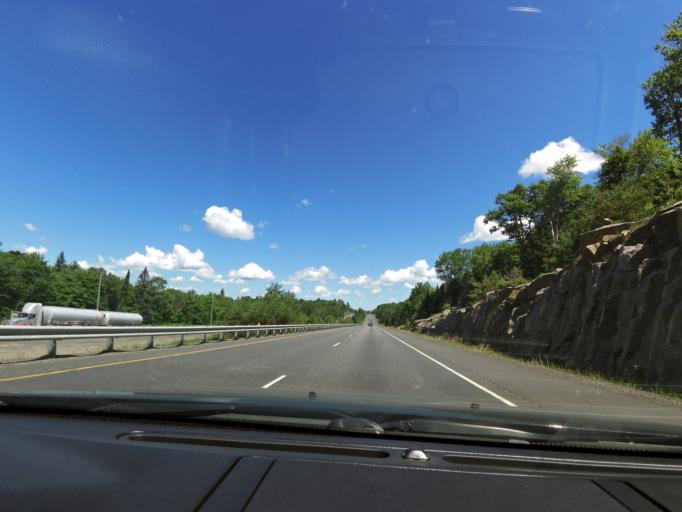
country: CA
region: Ontario
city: Bracebridge
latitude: 45.1642
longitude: -79.3114
